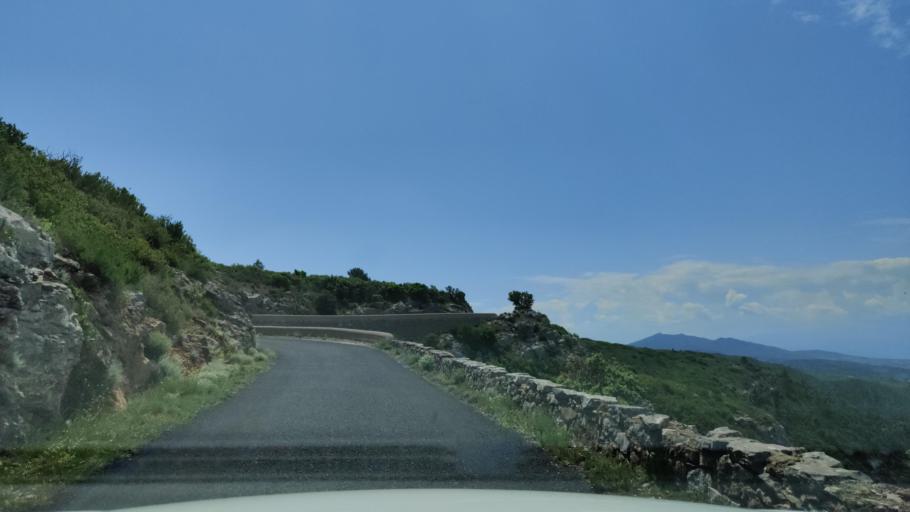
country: FR
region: Languedoc-Roussillon
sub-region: Departement des Pyrenees-Orientales
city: Estagel
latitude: 42.7960
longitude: 2.7243
